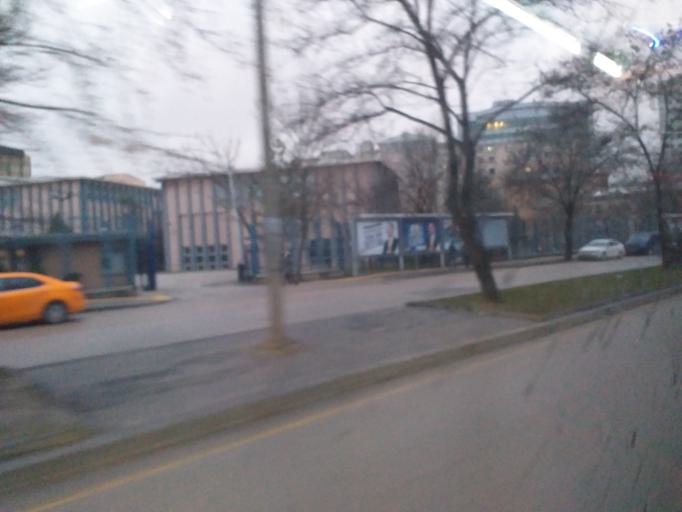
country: TR
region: Ankara
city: Ankara
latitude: 39.9339
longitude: 32.8273
